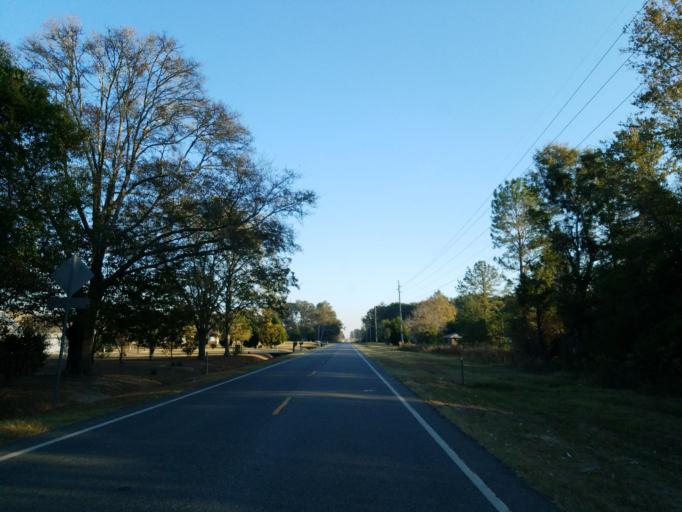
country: US
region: Georgia
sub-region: Crisp County
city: Cordele
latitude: 31.9317
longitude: -83.7273
